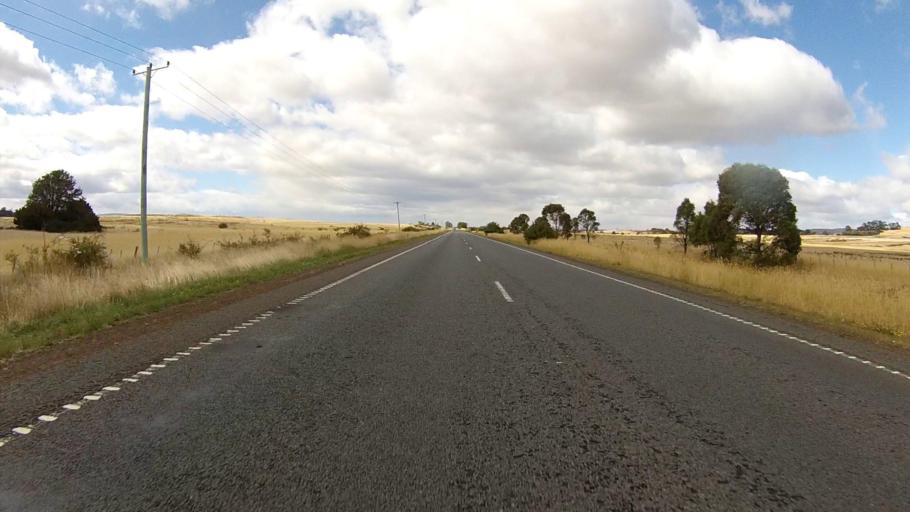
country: AU
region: Tasmania
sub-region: Northern Midlands
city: Evandale
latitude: -41.8540
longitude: 147.4526
